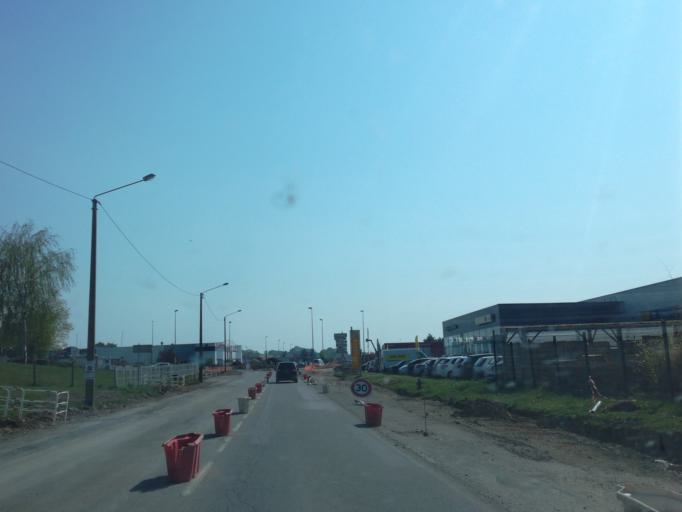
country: FR
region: Brittany
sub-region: Departement du Morbihan
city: Le Sourn
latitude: 48.0421
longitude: -2.9607
